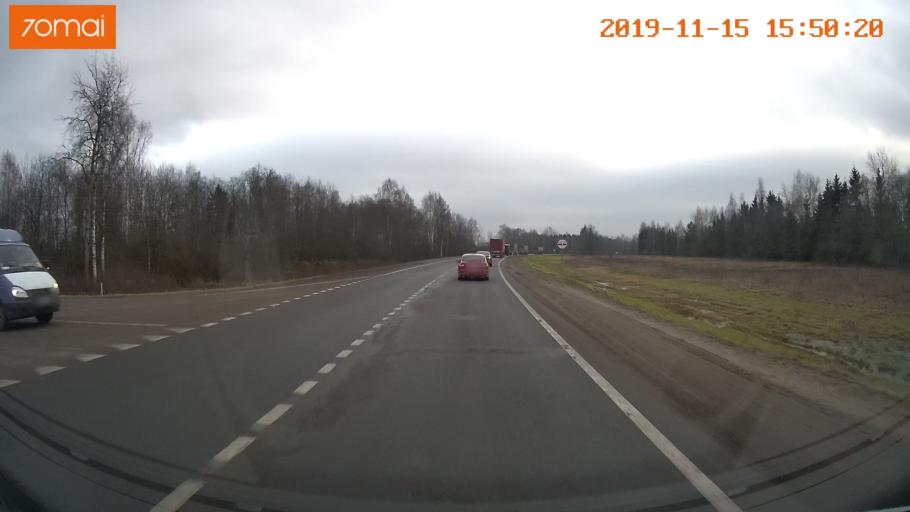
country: RU
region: Jaroslavl
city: Yaroslavl
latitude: 57.9065
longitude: 40.0131
